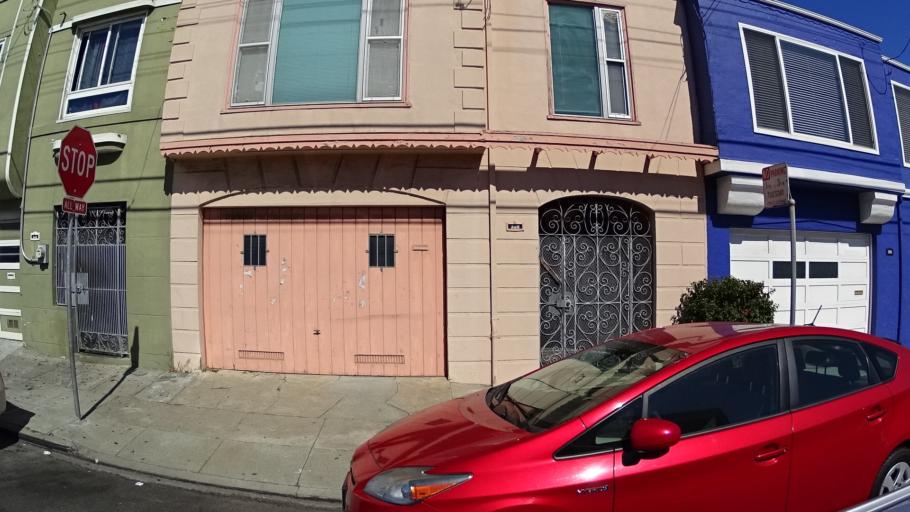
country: US
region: California
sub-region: San Francisco County
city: San Francisco
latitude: 37.7313
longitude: -122.3966
